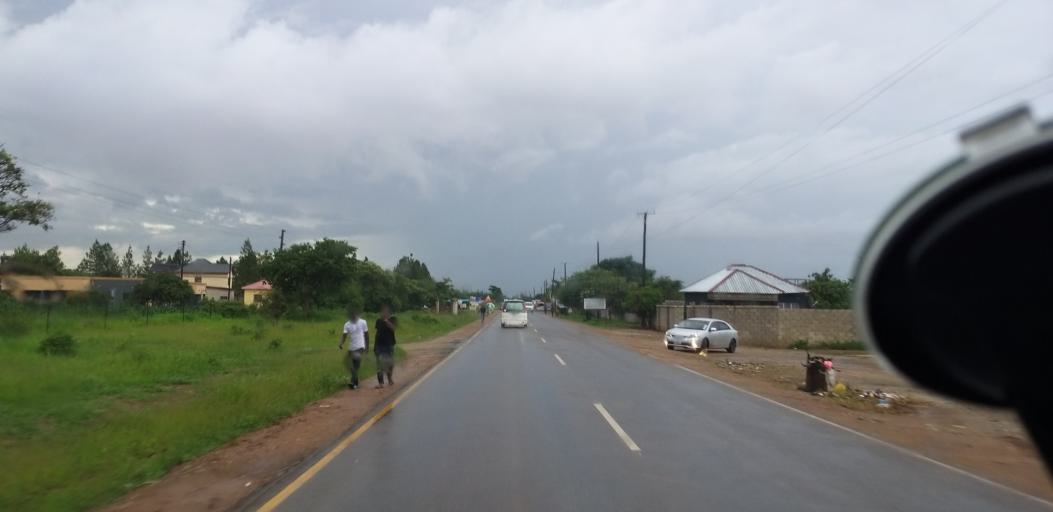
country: ZM
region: Lusaka
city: Lusaka
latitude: -15.4786
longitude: 28.3159
